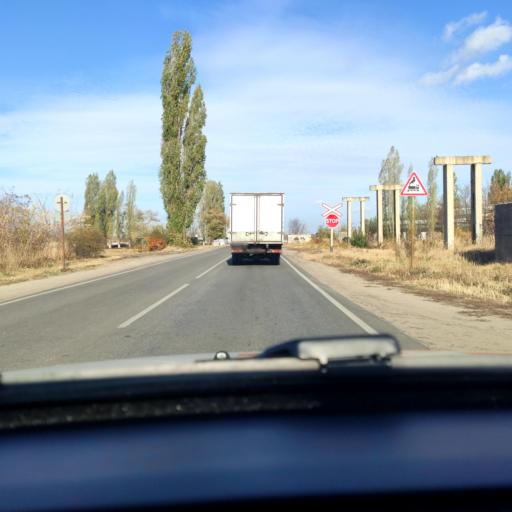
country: RU
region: Voronezj
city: Shilovo
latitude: 51.5703
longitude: 39.1386
